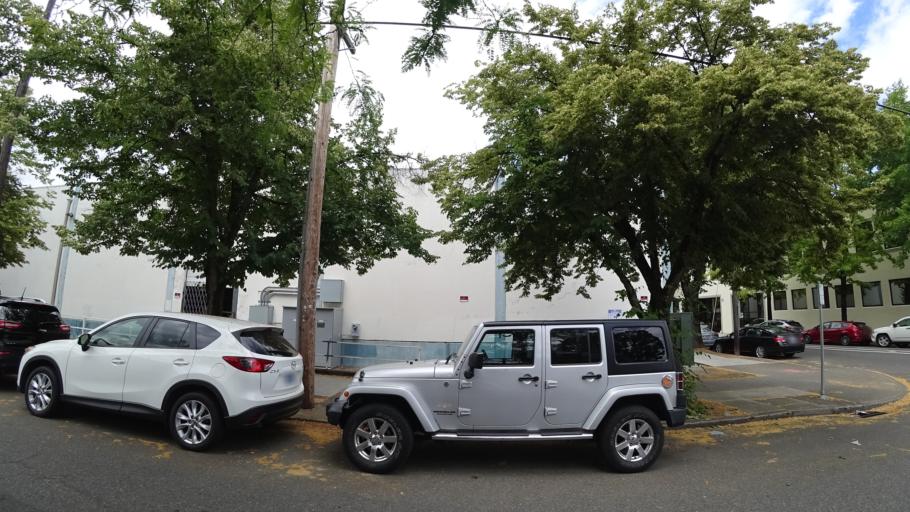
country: US
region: Oregon
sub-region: Multnomah County
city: Portland
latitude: 45.5328
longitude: -122.6899
